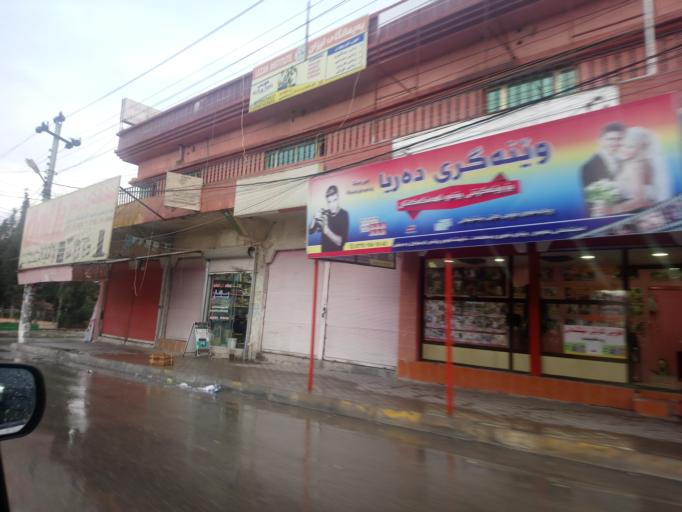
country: IQ
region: As Sulaymaniyah
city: Qeladize
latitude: 36.1833
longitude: 45.1239
